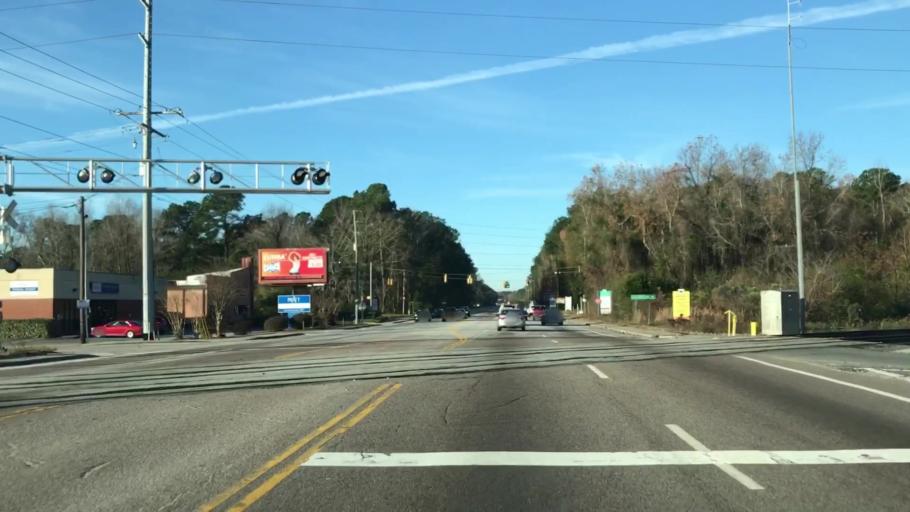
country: US
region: South Carolina
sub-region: Berkeley County
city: Ladson
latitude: 32.9856
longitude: -80.1101
